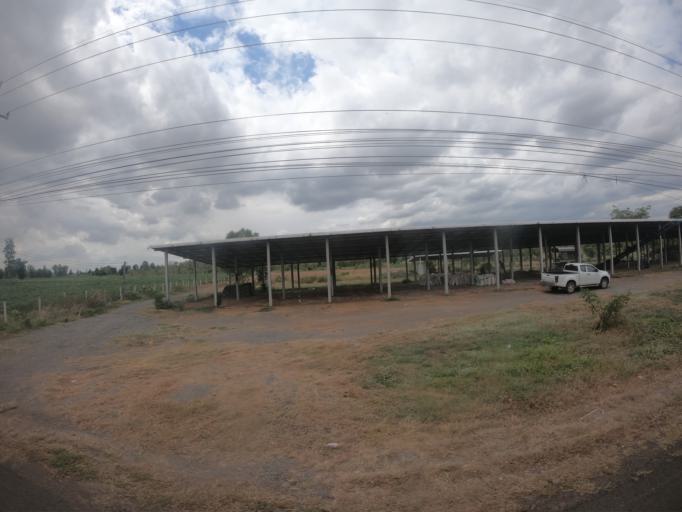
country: TH
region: Buriram
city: Nang Rong
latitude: 14.6431
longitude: 102.6847
